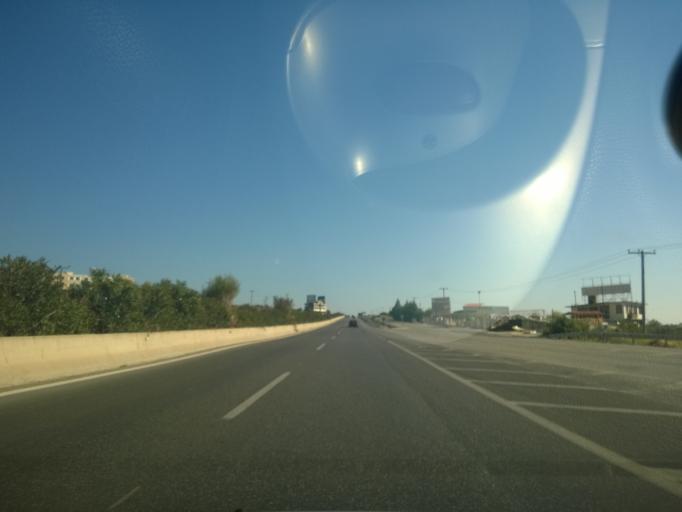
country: GR
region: Central Macedonia
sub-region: Nomos Chalkidikis
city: Lakkoma
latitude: 40.3588
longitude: 23.0531
